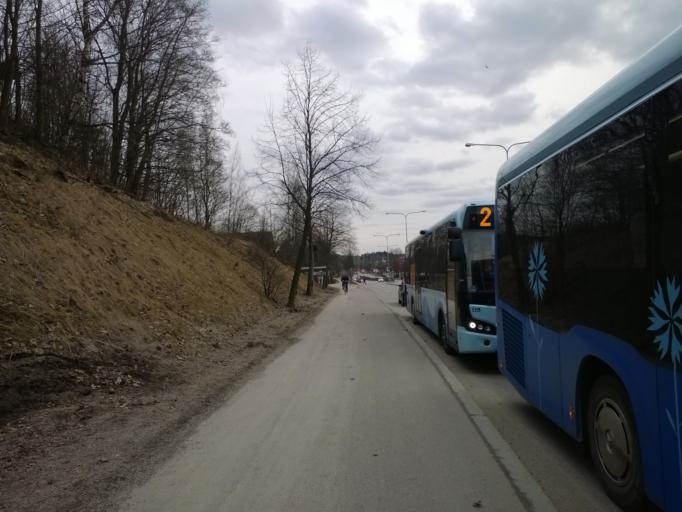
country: FI
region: Paijanne Tavastia
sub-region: Lahti
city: Lahti
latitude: 60.9754
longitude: 25.6587
